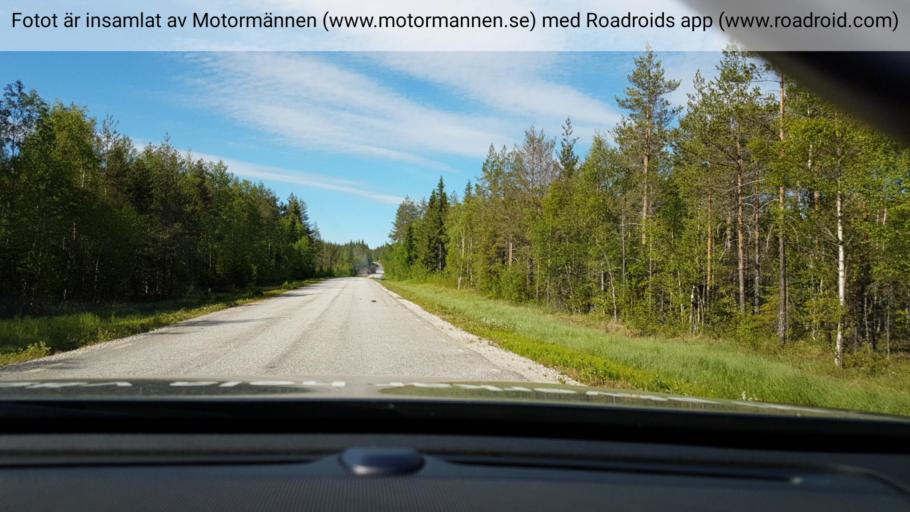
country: SE
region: Vaesterbotten
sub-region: Bjurholms Kommun
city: Bjurholm
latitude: 63.9800
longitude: 19.3286
